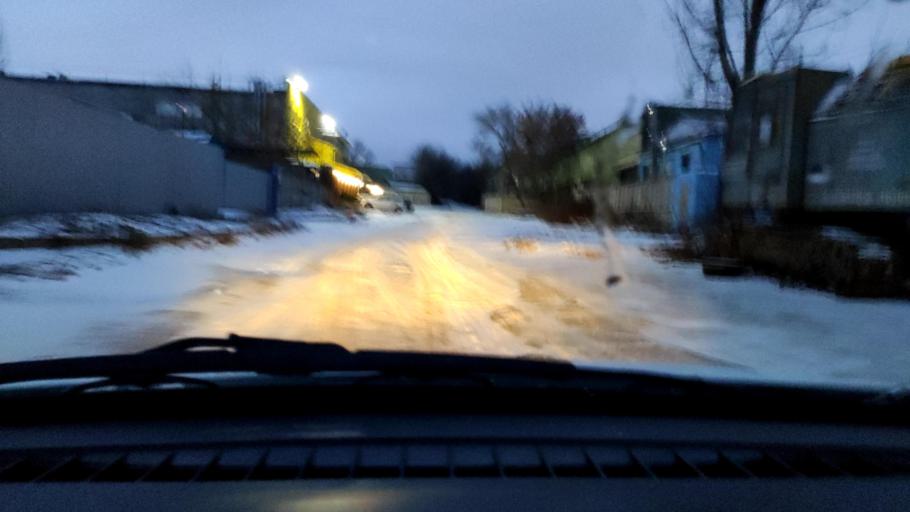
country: RU
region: Voronezj
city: Voronezh
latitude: 51.6854
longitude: 39.1465
